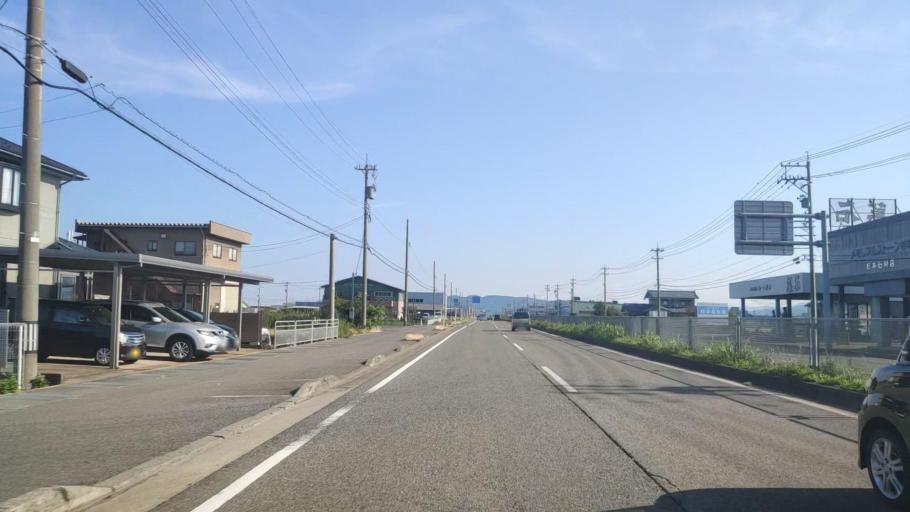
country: JP
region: Fukui
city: Maruoka
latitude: 36.1602
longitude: 136.2640
